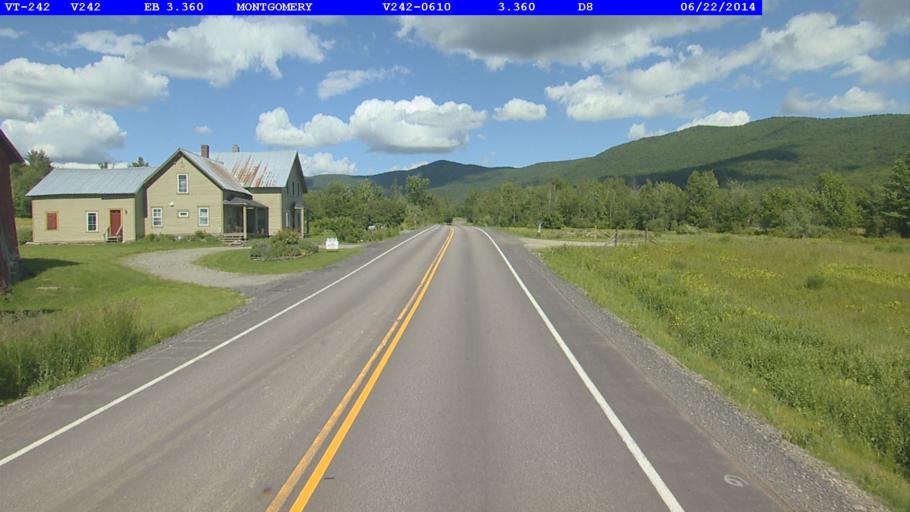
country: US
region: Vermont
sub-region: Franklin County
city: Richford
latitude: 44.8833
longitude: -72.5461
